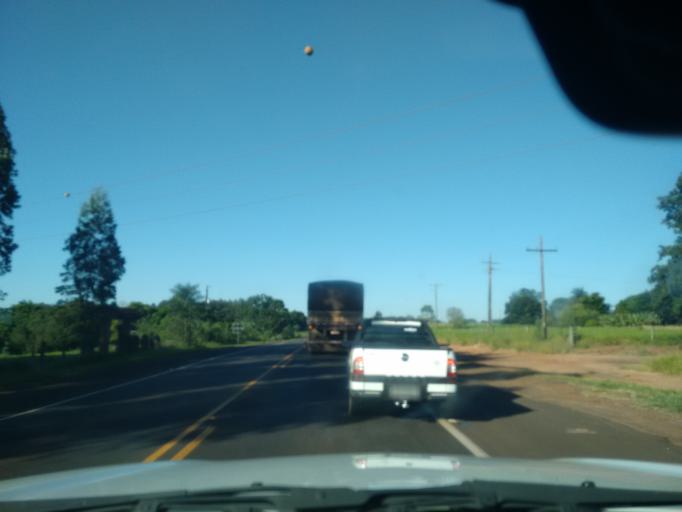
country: PY
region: Canindeyu
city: Salto del Guaira
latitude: -23.9613
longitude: -54.3211
